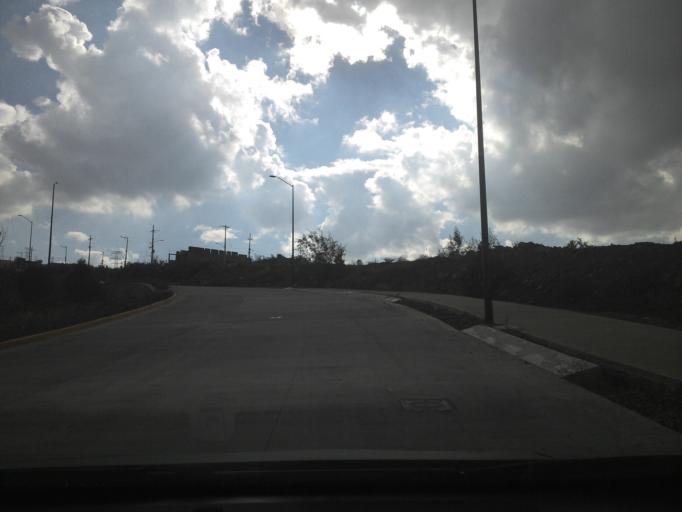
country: MX
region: Jalisco
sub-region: Tlajomulco de Zuniga
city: Altus Bosques
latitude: 20.6129
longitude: -103.3635
